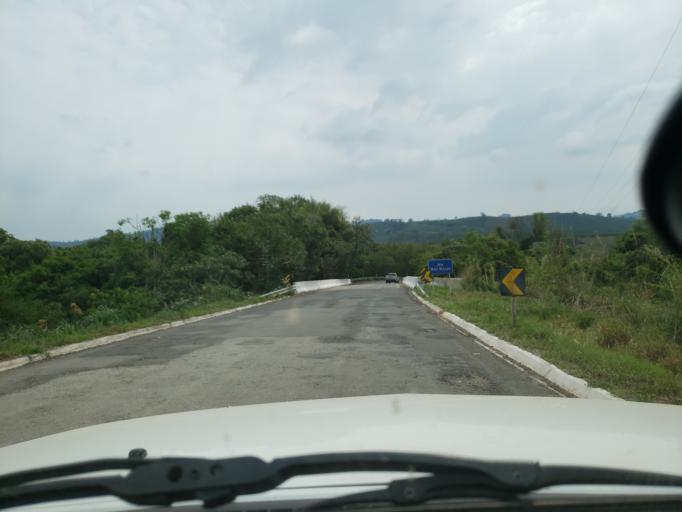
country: BR
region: Minas Gerais
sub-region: Jacutinga
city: Jacutinga
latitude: -22.2700
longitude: -46.6051
